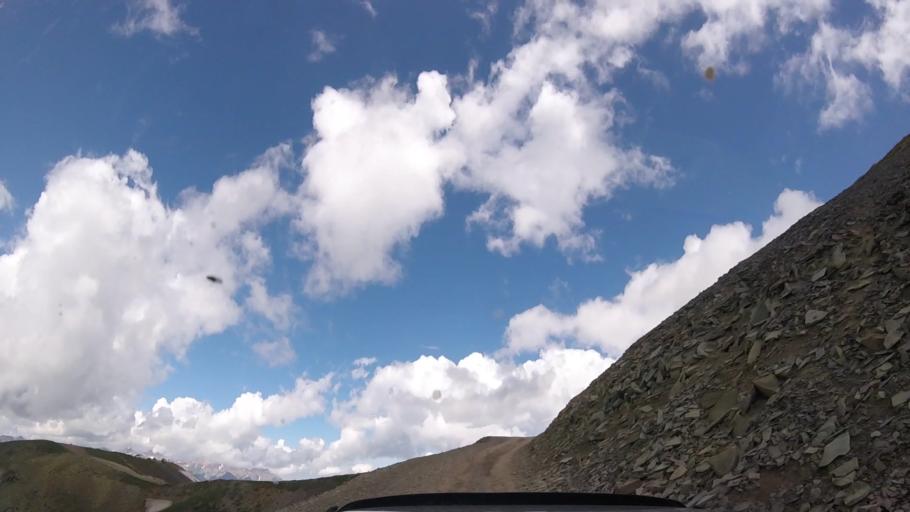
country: US
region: Colorado
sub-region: Ouray County
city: Ouray
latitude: 37.9693
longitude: -107.5900
